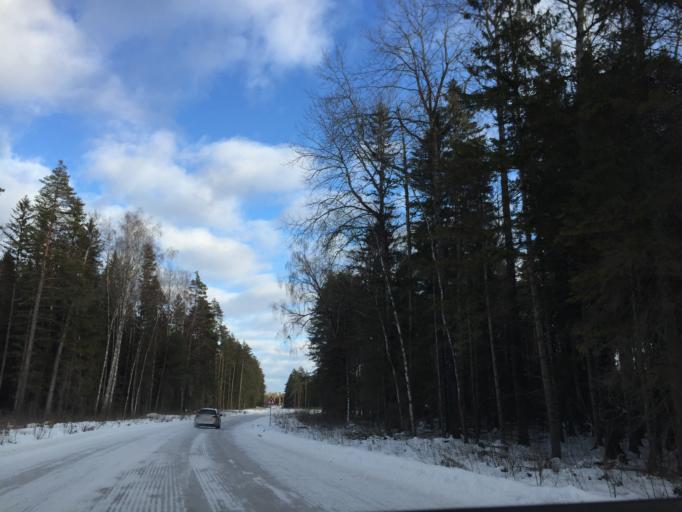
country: LV
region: Ogre
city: Jumprava
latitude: 56.5856
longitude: 24.9636
